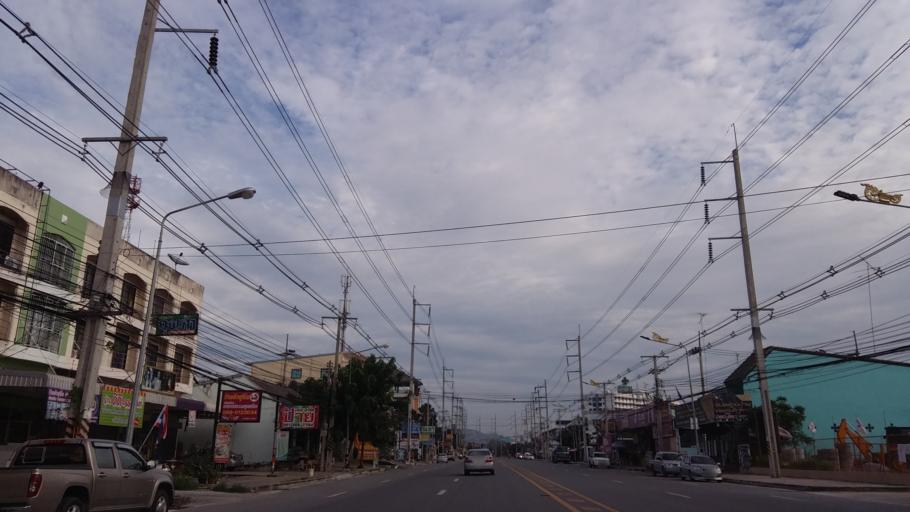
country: TH
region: Chon Buri
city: Chon Buri
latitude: 13.3215
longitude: 100.9459
